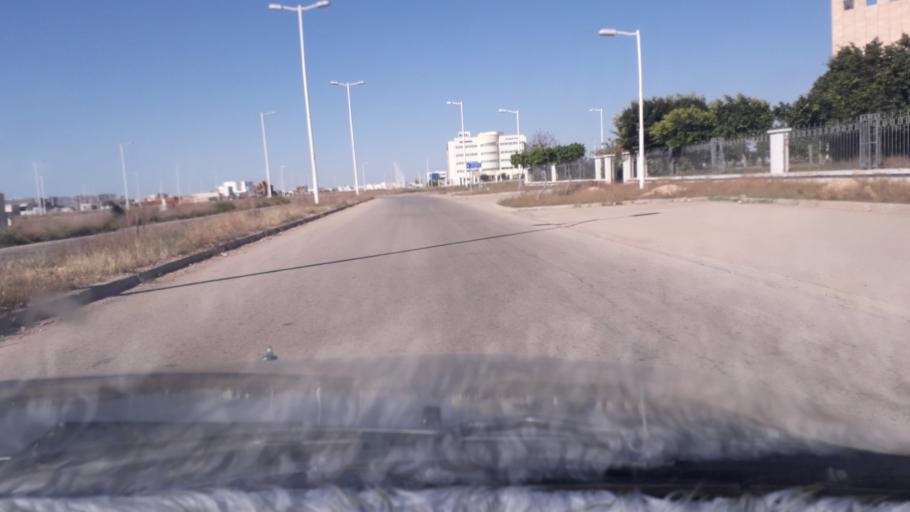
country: TN
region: Safaqis
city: Al Qarmadah
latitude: 34.8359
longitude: 10.7550
